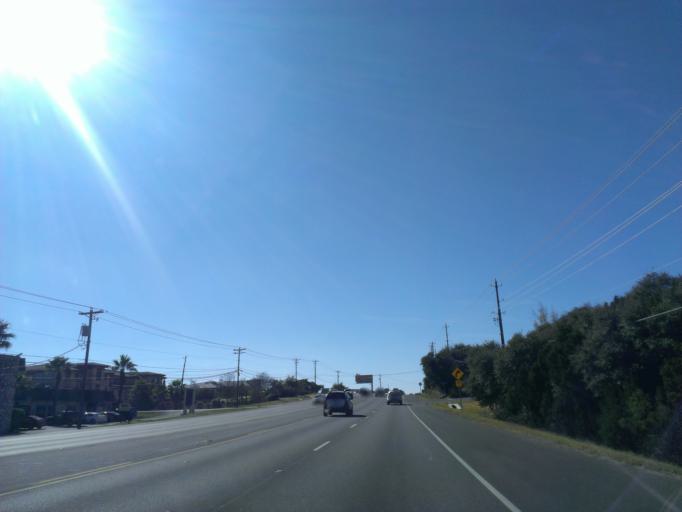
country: US
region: Texas
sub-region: Travis County
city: Lakeway
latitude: 30.3625
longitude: -97.9530
